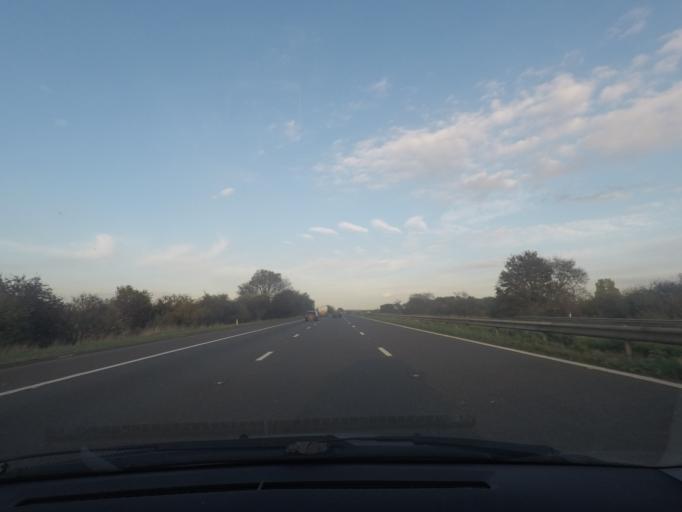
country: GB
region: England
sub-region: North Lincolnshire
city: Brigg
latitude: 53.5570
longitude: -0.5061
